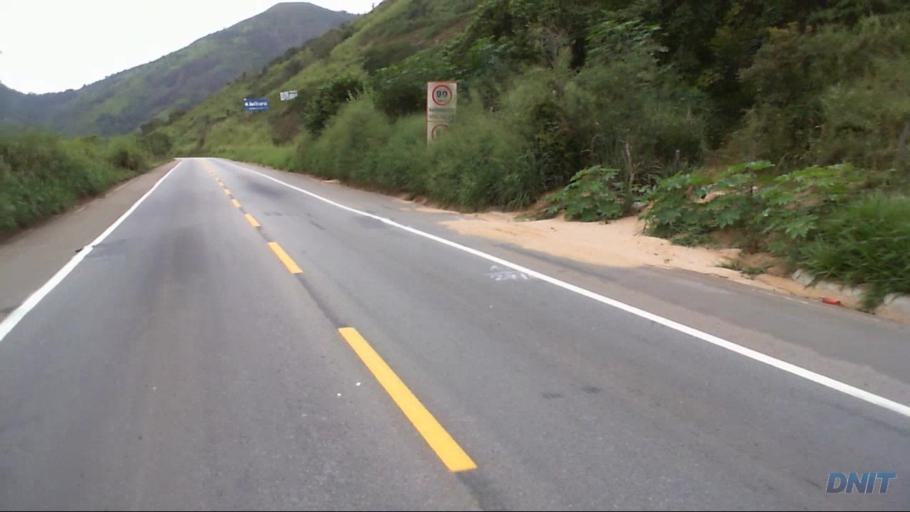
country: BR
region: Minas Gerais
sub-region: Timoteo
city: Timoteo
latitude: -19.5791
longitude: -42.7237
